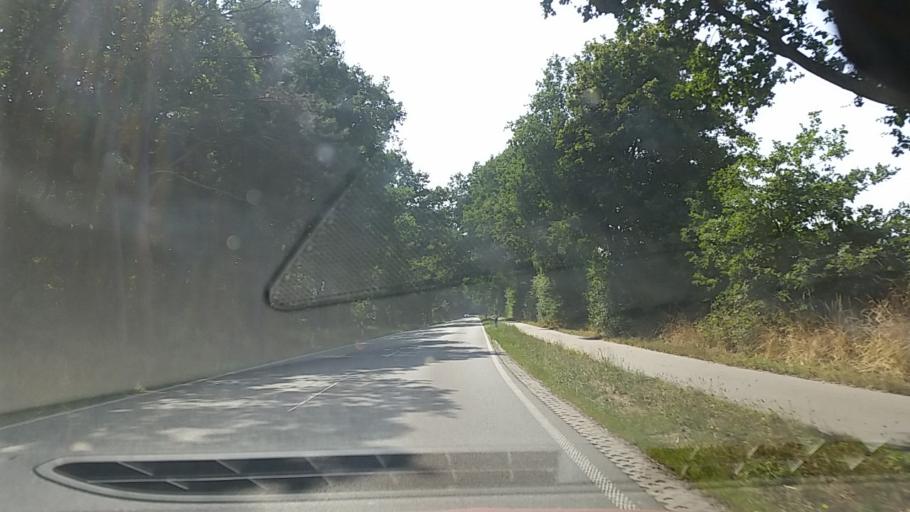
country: DE
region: Schleswig-Holstein
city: Grande
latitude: 53.5778
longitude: 10.3805
